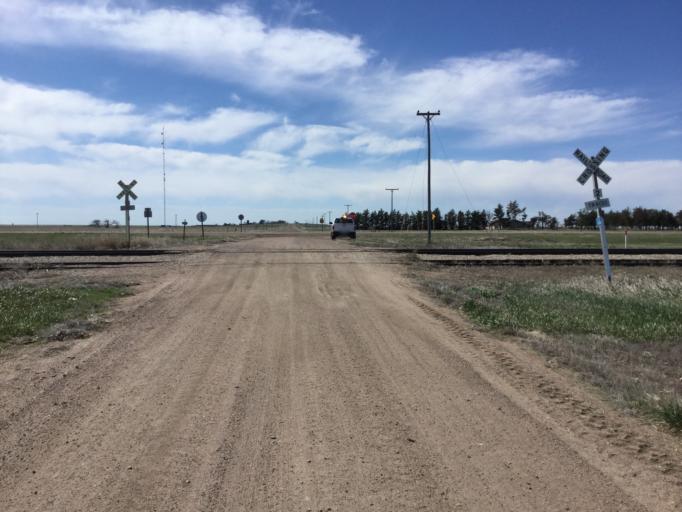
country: US
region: Kansas
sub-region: Sherman County
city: Goodland
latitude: 39.3403
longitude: -101.5401
